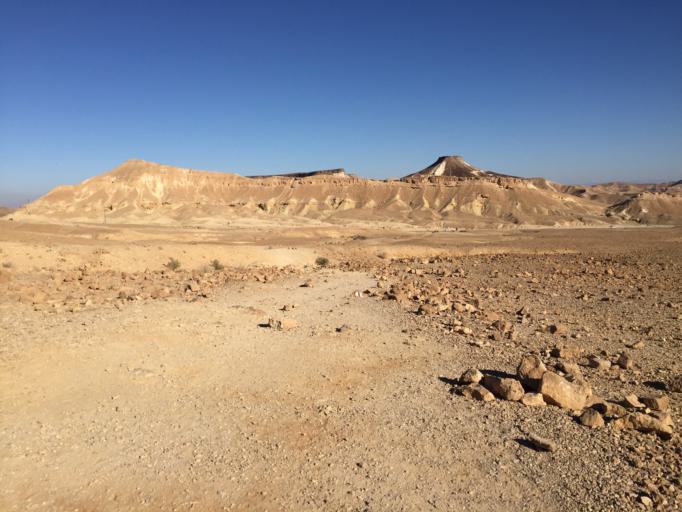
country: IL
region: Southern District
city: Mitzpe Ramon
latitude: 30.5767
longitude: 34.8795
